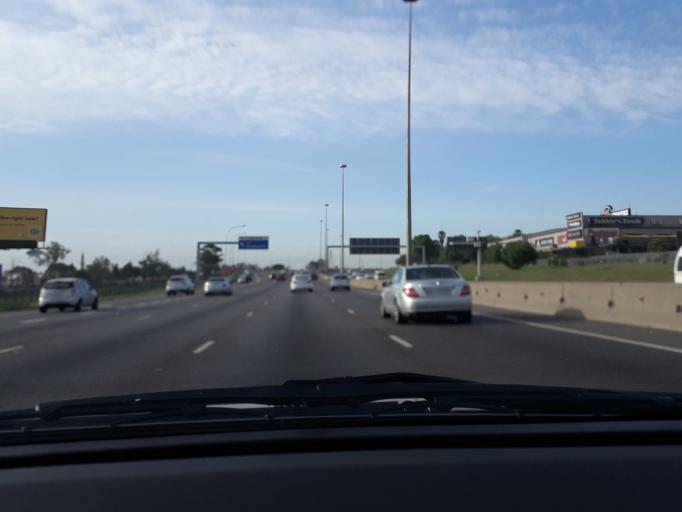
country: ZA
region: Gauteng
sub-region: City of Johannesburg Metropolitan Municipality
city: Midrand
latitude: -26.0553
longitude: 28.0940
